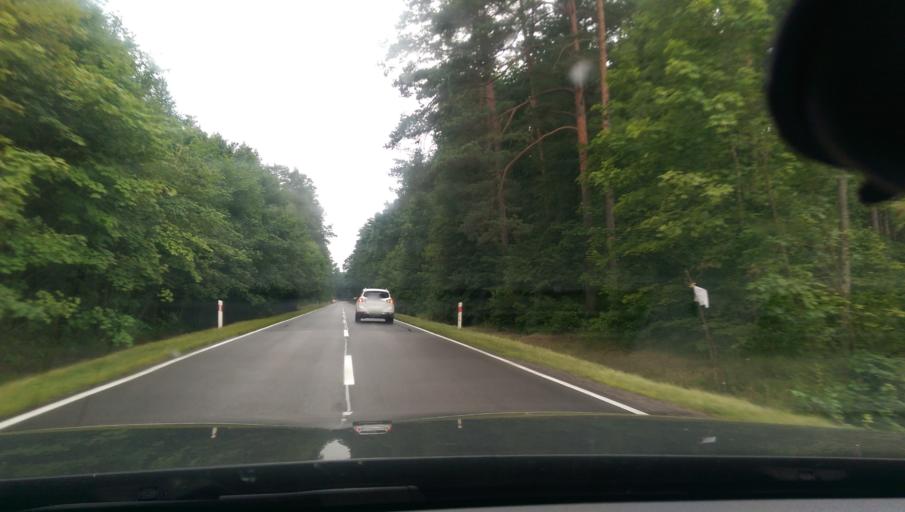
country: PL
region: Warmian-Masurian Voivodeship
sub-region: Powiat szczycienski
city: Szczytno
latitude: 53.5284
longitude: 20.9806
